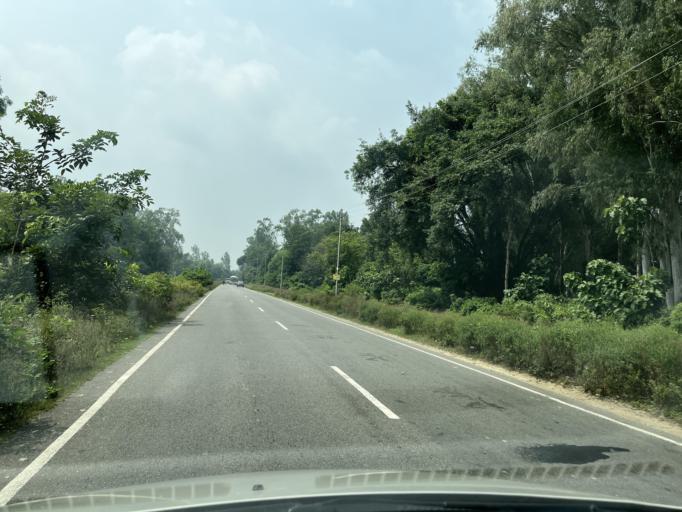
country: IN
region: Uttarakhand
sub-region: Haridwar
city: Sultanpur
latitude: 29.7531
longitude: 78.2648
